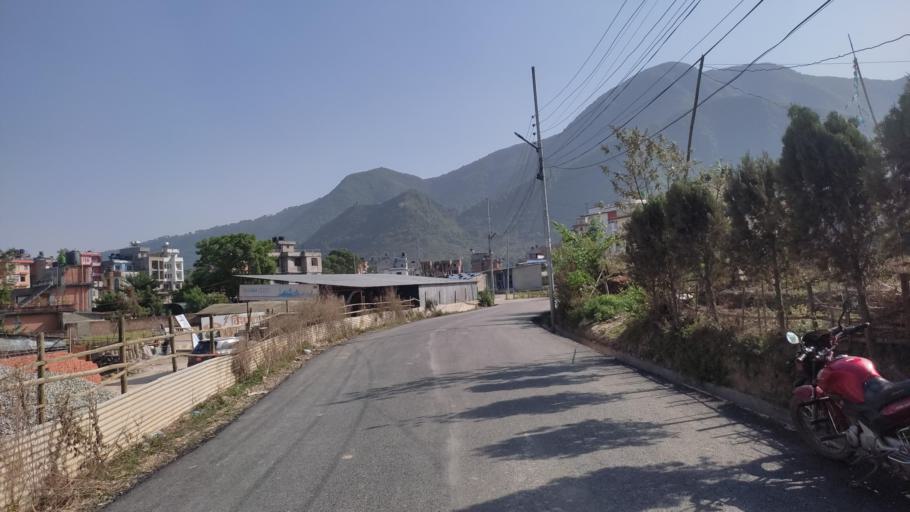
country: NP
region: Central Region
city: Kirtipur
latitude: 27.6687
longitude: 85.2713
